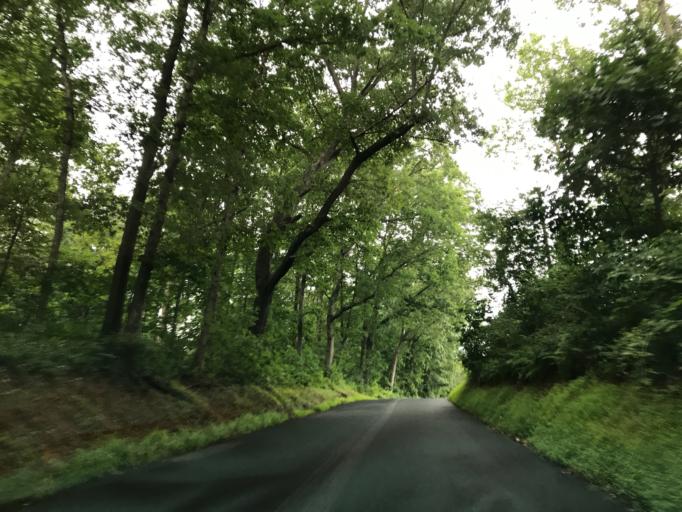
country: US
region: Pennsylvania
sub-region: York County
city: New Freedom
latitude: 39.6754
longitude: -76.7396
